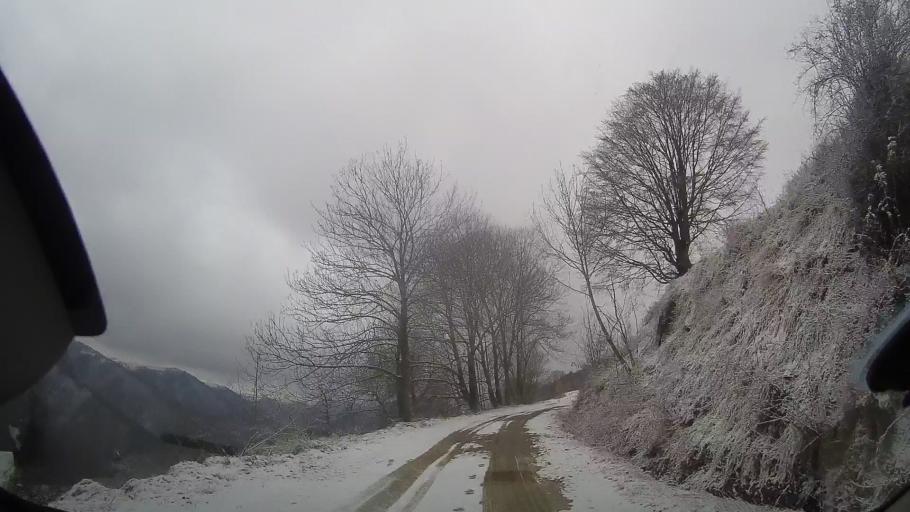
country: RO
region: Cluj
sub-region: Comuna Maguri-Racatau
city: Maguri-Racatau
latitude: 46.6632
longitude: 23.1869
